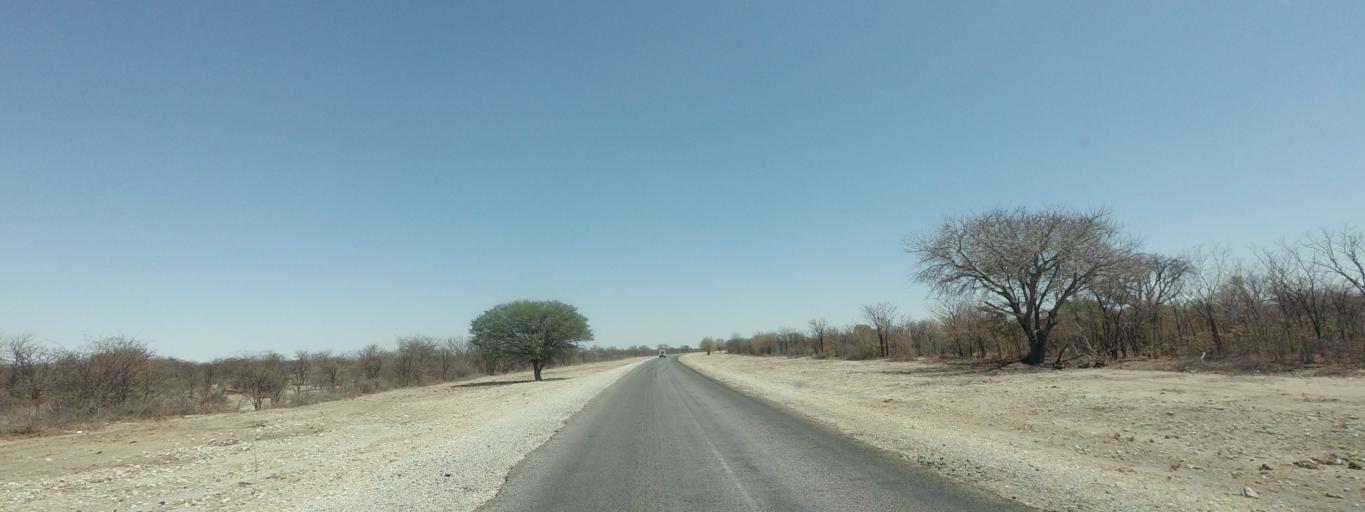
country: BW
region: Central
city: Nata
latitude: -20.3809
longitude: 26.3282
